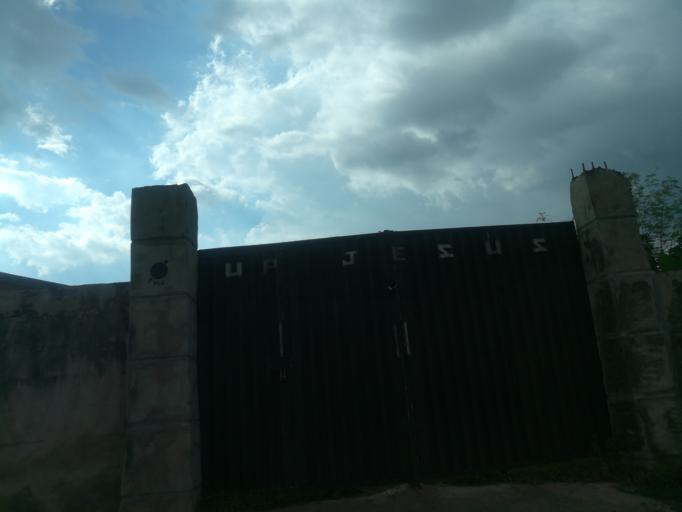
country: NG
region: Oyo
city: Ibadan
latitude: 7.4016
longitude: 3.8362
